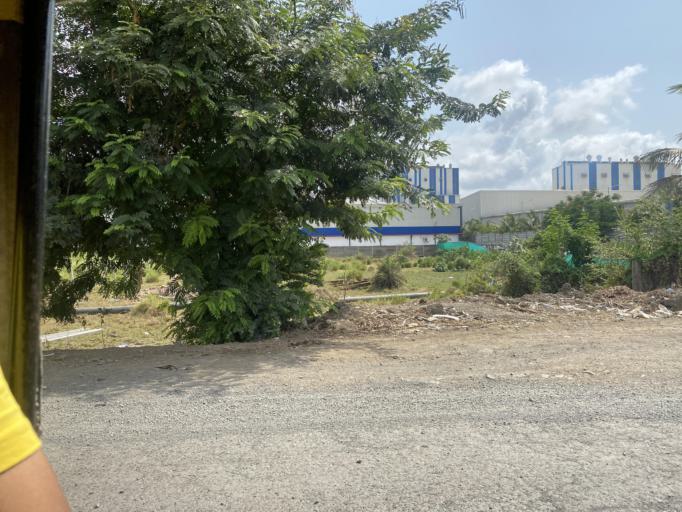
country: IN
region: Gujarat
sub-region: Valsad
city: Vapi
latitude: 20.2833
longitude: 72.8582
